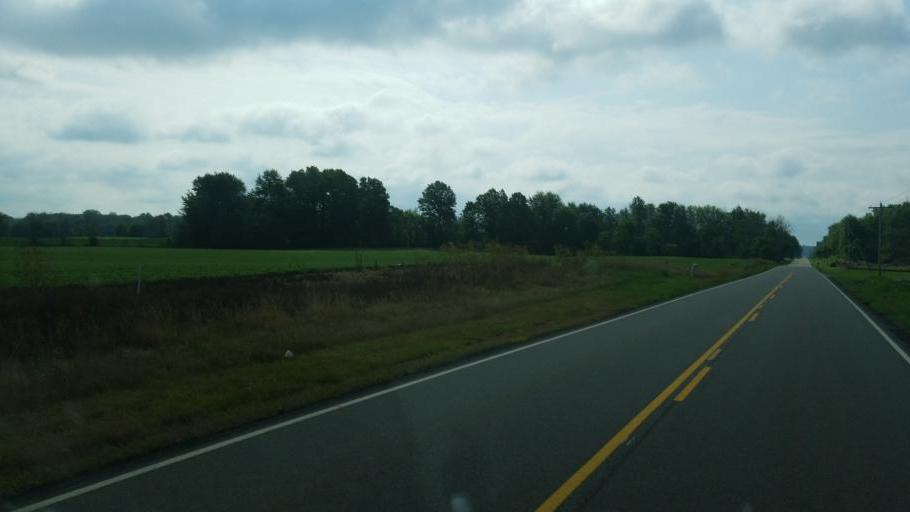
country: US
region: Ohio
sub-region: Licking County
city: Utica
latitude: 40.2344
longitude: -82.5693
